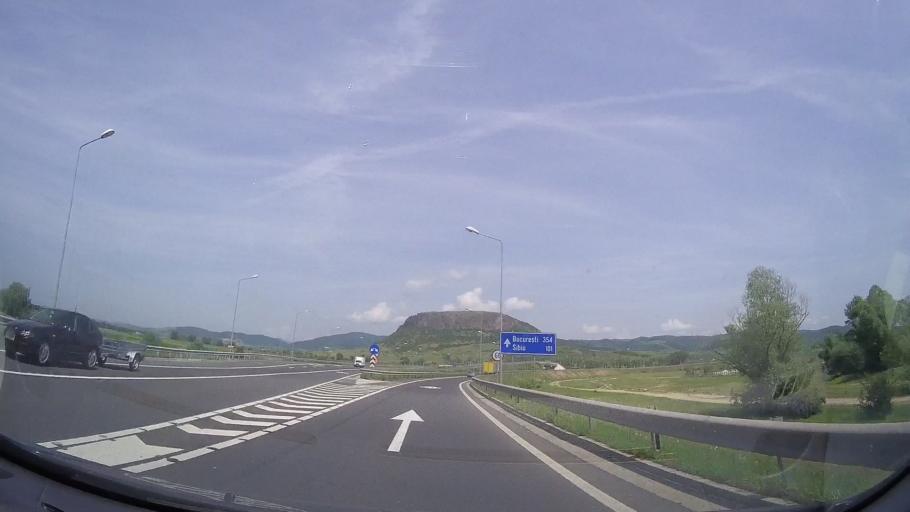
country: RO
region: Hunedoara
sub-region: Oras Simeria
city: Simeria
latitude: 45.8442
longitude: 23.0449
